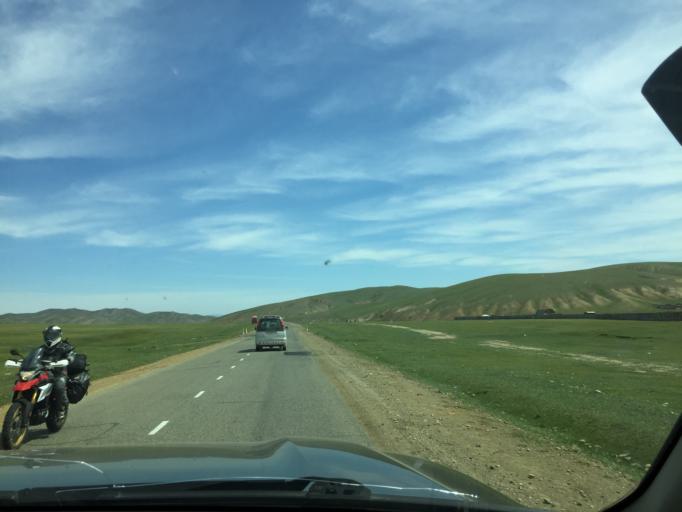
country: MN
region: Central Aimak
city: Bornuur
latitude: 48.6668
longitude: 106.1317
